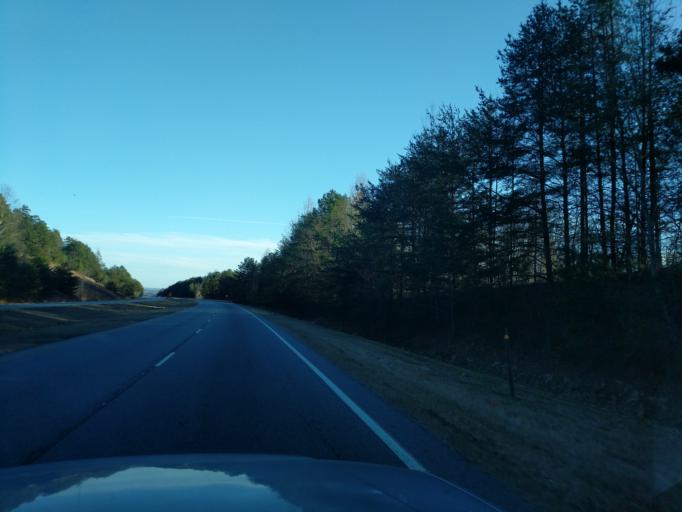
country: US
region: Georgia
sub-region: Stephens County
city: Toccoa
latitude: 34.5654
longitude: -83.3976
